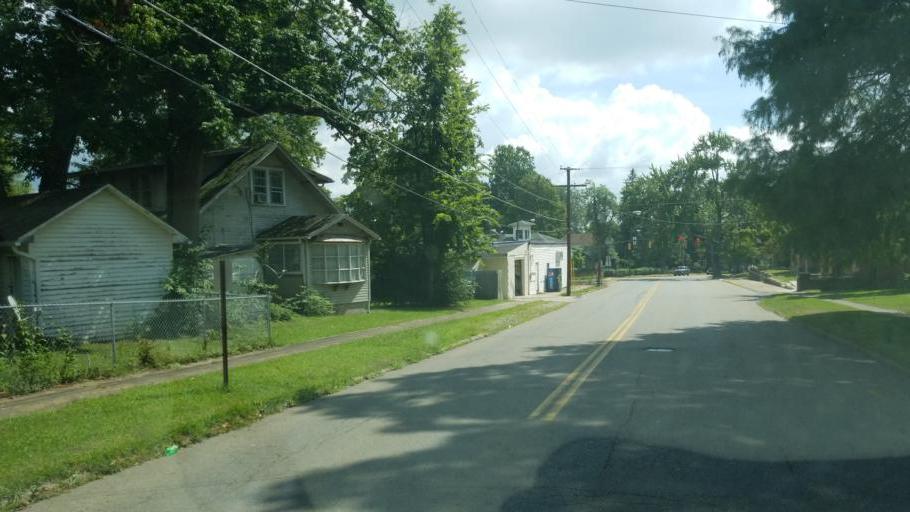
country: US
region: Ohio
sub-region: Knox County
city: Mount Vernon
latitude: 40.4010
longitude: -82.4853
